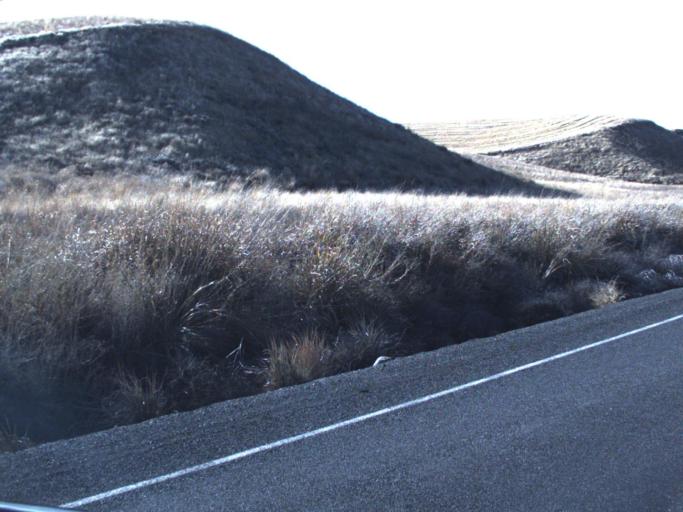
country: US
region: Washington
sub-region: Adams County
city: Ritzville
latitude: 46.8187
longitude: -118.3139
